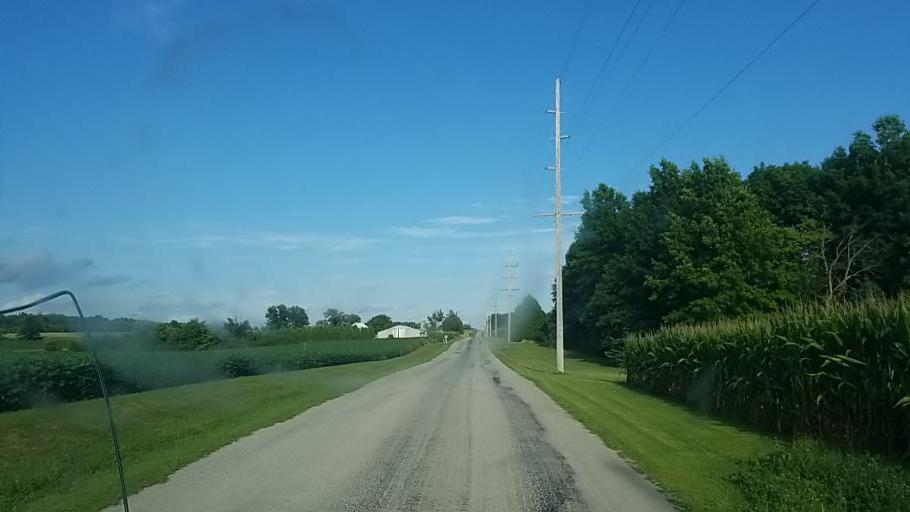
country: US
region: Ohio
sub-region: Wyandot County
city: Upper Sandusky
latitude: 40.8147
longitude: -83.1824
